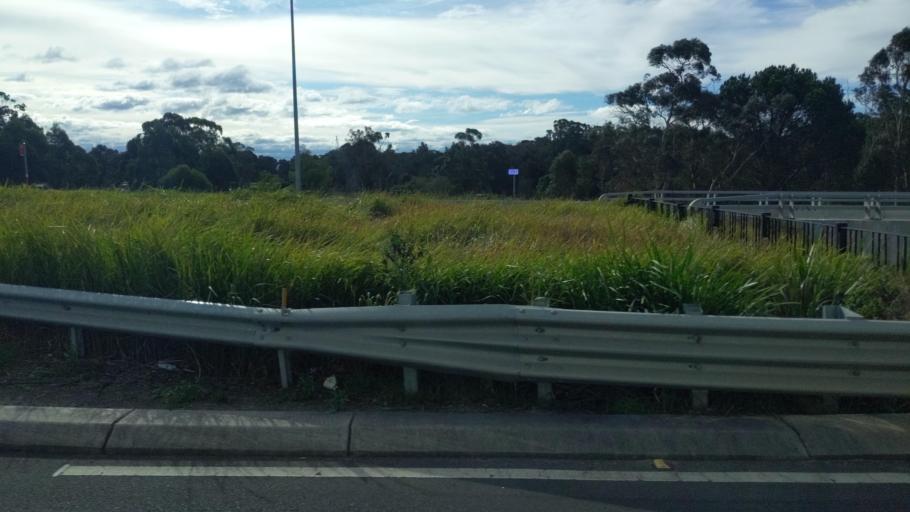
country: AU
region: New South Wales
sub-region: Blacktown
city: Riverstone
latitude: -33.7041
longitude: 150.8600
